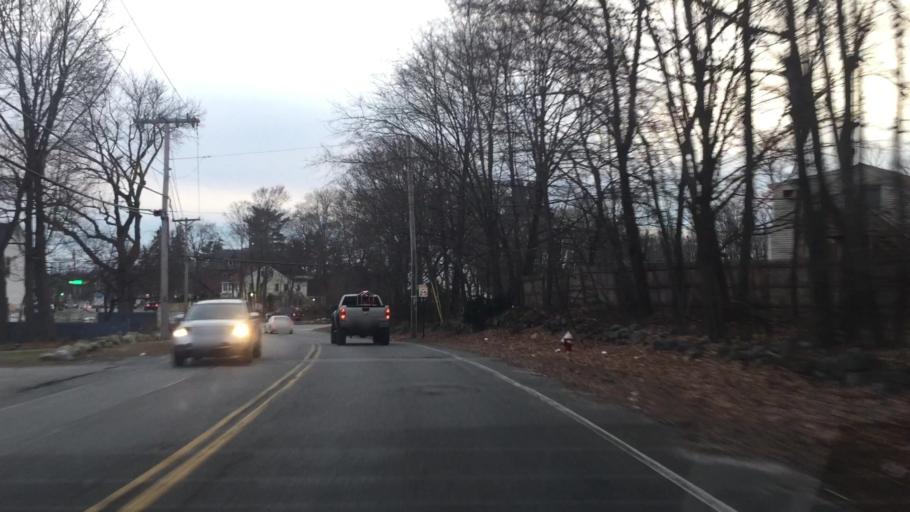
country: US
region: Massachusetts
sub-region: Middlesex County
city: Dracut
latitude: 42.6852
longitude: -71.3550
